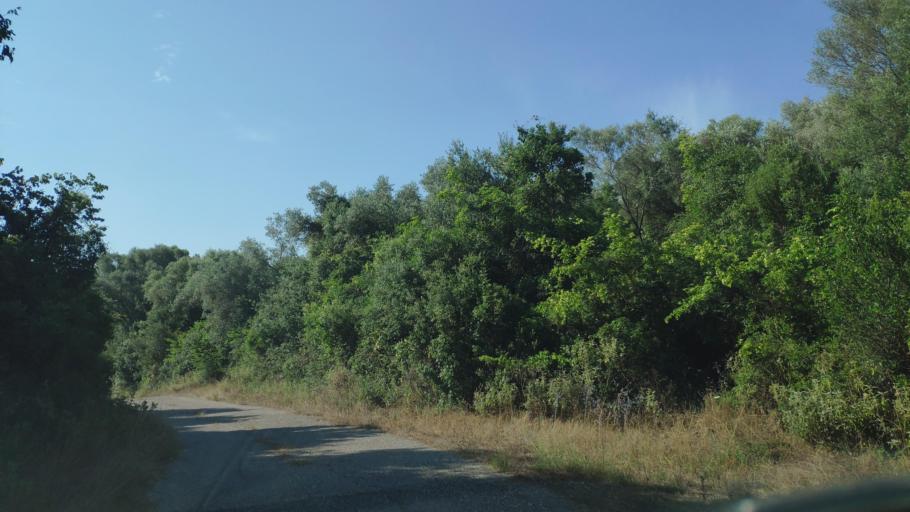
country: GR
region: West Greece
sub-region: Nomos Aitolias kai Akarnanias
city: Fitiai
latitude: 38.6963
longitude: 21.2097
